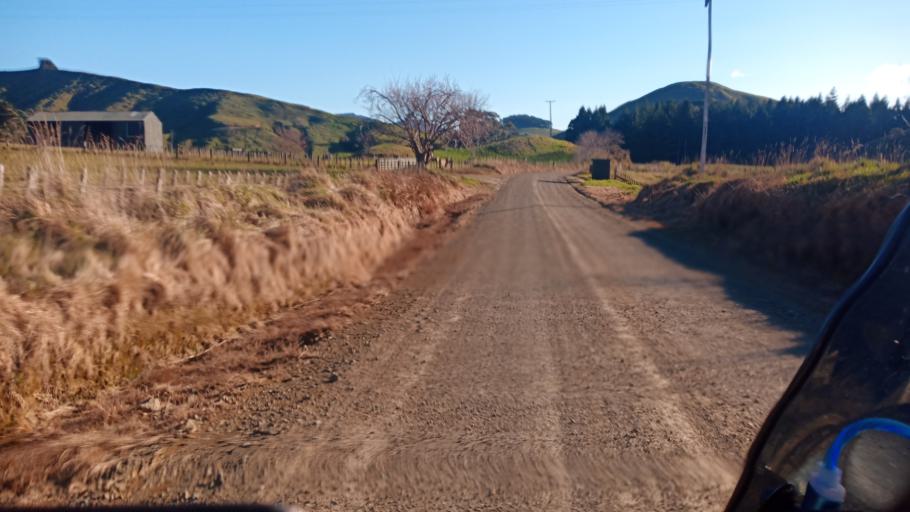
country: NZ
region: Bay of Plenty
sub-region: Opotiki District
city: Opotiki
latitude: -38.4589
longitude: 177.4287
